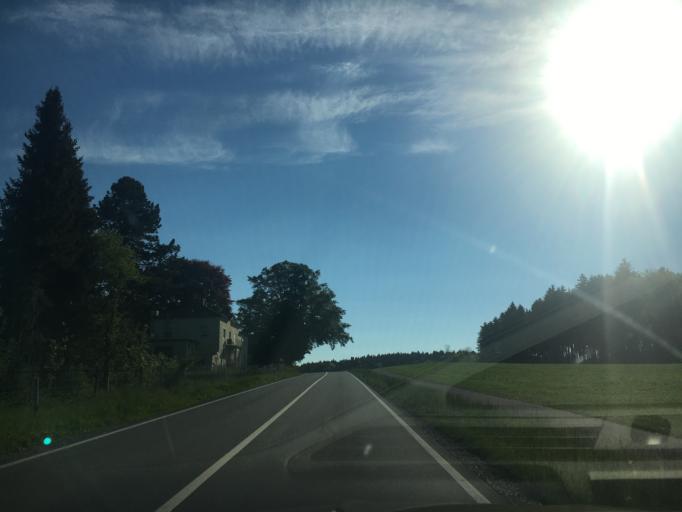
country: DE
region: Bavaria
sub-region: Upper Bavaria
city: Nussdorf
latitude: 47.9142
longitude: 12.5649
